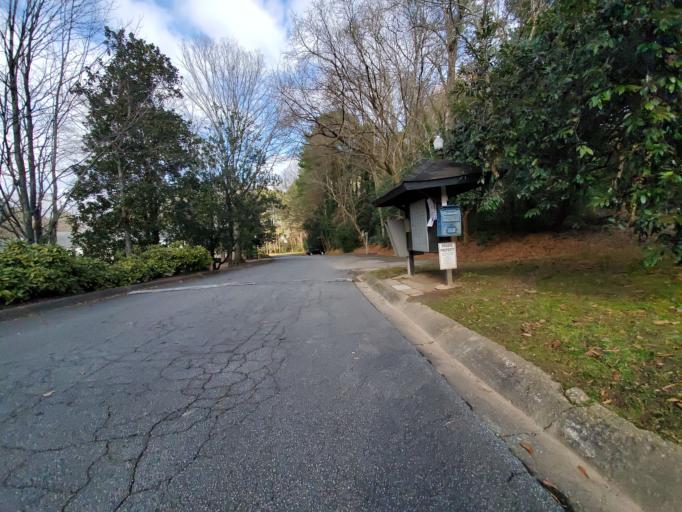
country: US
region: Georgia
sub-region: DeKalb County
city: North Decatur
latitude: 33.8018
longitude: -84.3014
